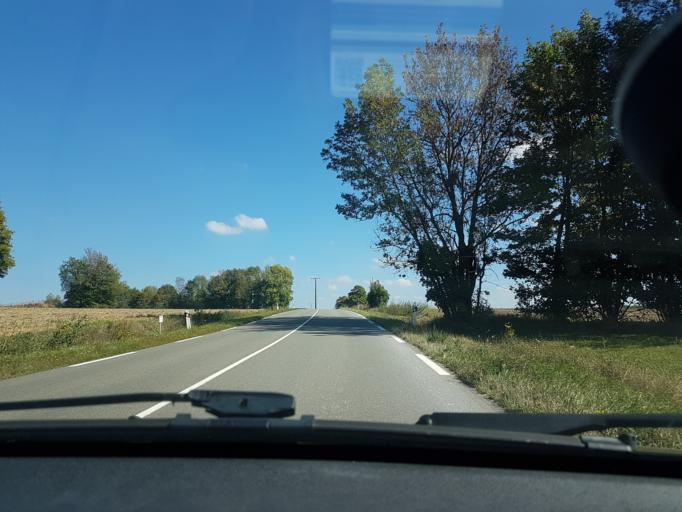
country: FR
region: Franche-Comte
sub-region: Territoire de Belfort
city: Chevremont
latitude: 47.6394
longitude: 6.9065
